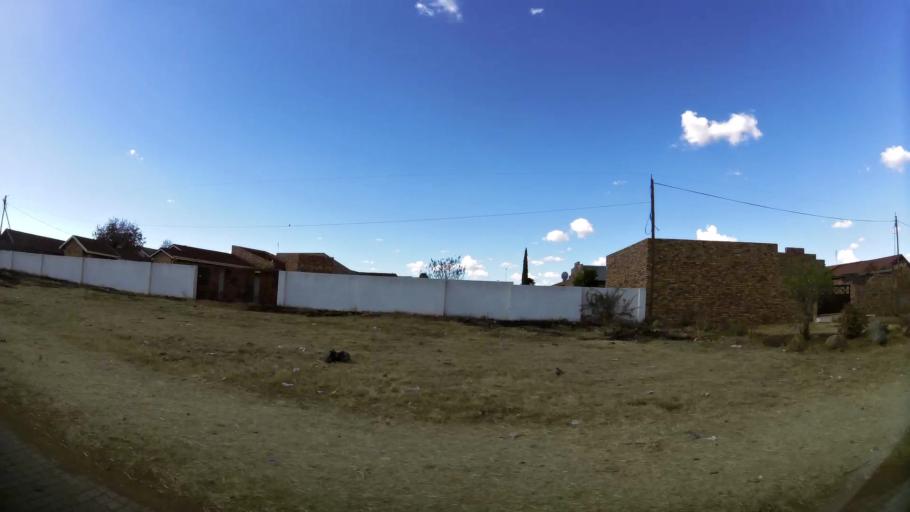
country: ZA
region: North-West
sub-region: Dr Kenneth Kaunda District Municipality
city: Klerksdorp
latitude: -26.8735
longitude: 26.5817
